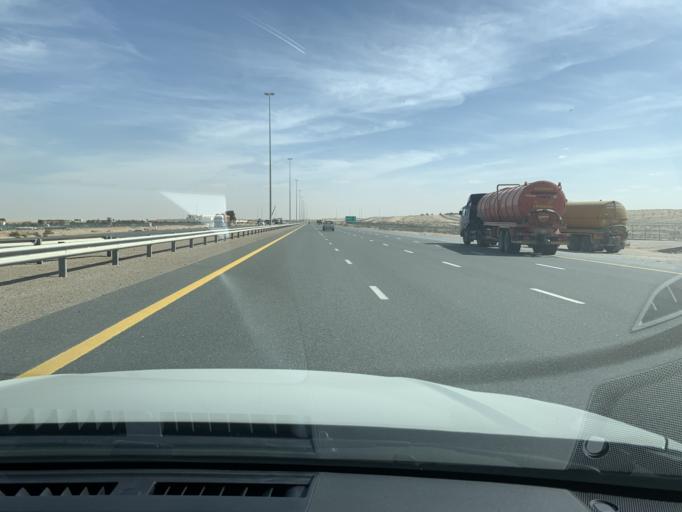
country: AE
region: Dubai
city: Dubai
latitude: 24.9554
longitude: 55.2828
